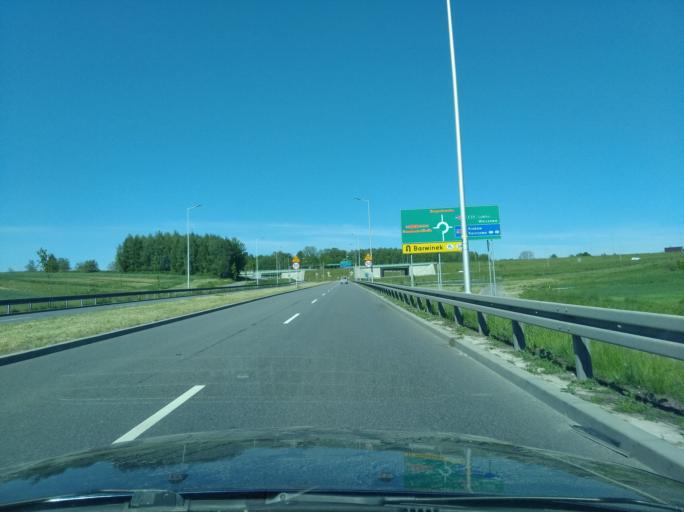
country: PL
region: Subcarpathian Voivodeship
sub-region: Powiat rzeszowski
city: Kielanowka
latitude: 50.0140
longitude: 21.9257
